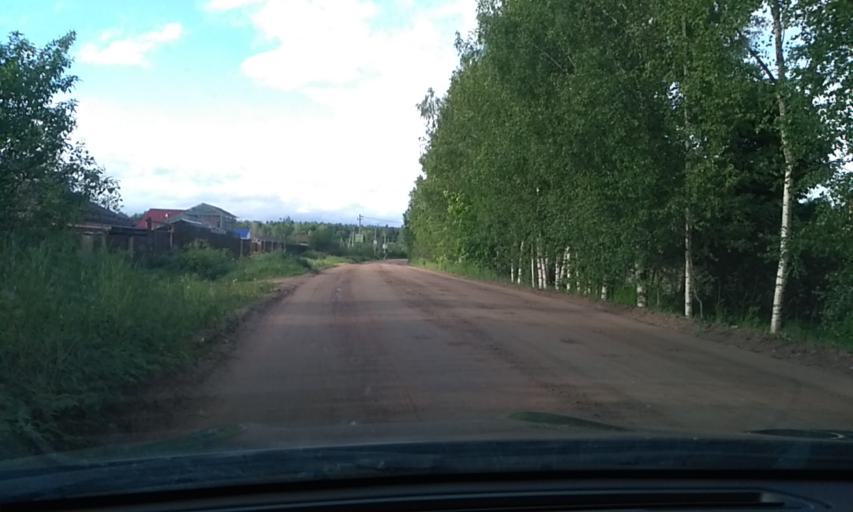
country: RU
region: Leningrad
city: Otradnoye
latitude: 59.8024
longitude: 30.8034
